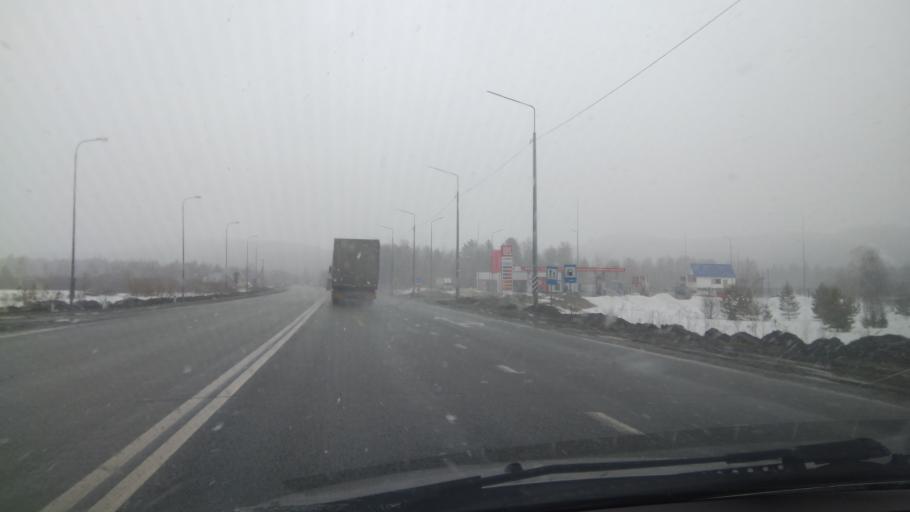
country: RU
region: Sverdlovsk
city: Arti
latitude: 56.7919
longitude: 58.6062
